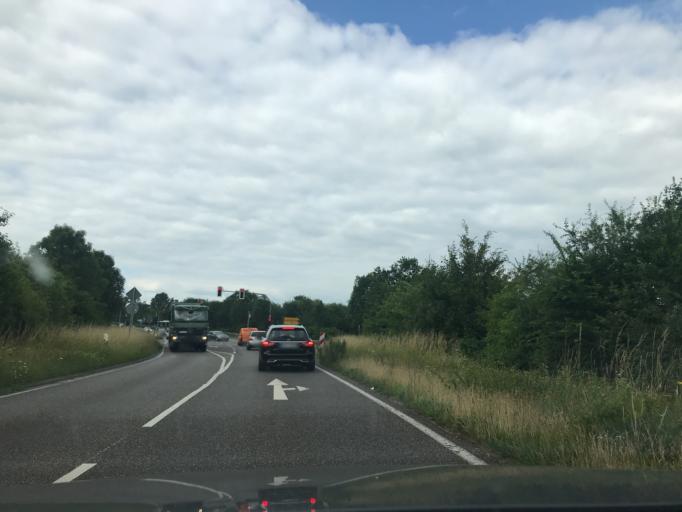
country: DE
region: North Rhine-Westphalia
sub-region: Regierungsbezirk Dusseldorf
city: Neuss
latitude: 51.1604
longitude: 6.7224
